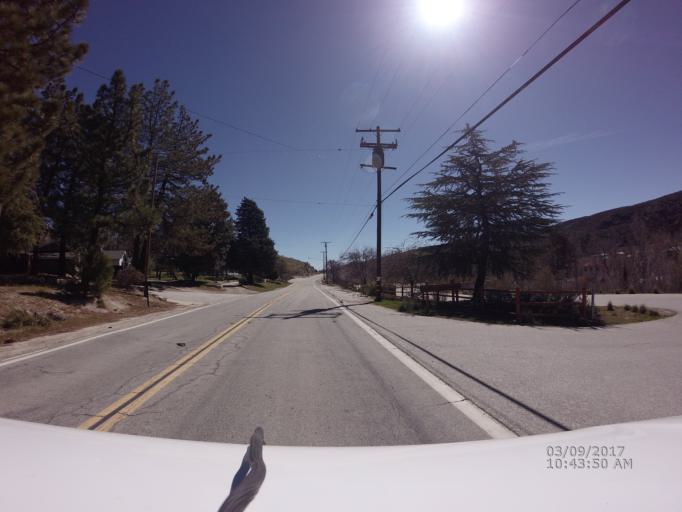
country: US
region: California
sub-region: Los Angeles County
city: Green Valley
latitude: 34.6734
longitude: -118.4309
